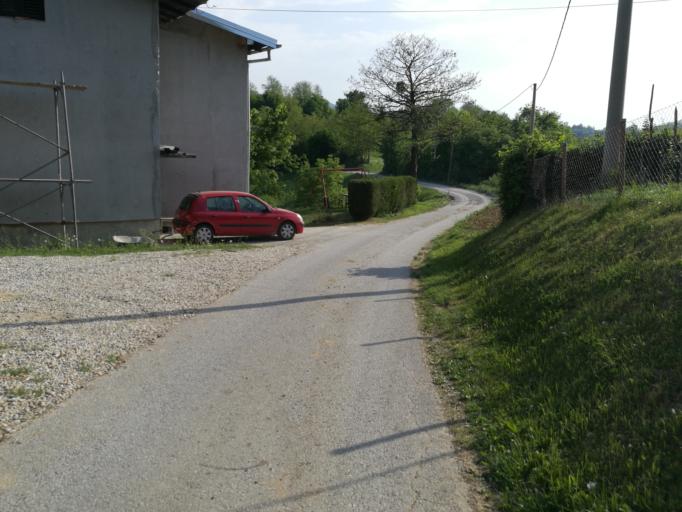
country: HR
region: Krapinsko-Zagorska
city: Radoboj
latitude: 46.2339
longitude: 15.9089
